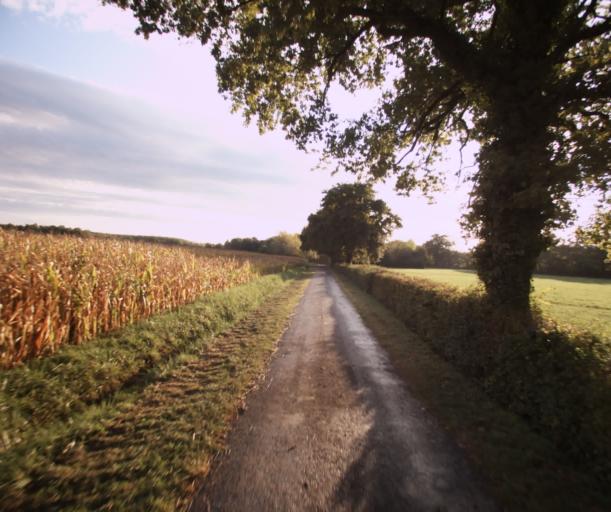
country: FR
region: Midi-Pyrenees
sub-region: Departement du Gers
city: Cazaubon
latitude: 43.9021
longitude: -0.0372
